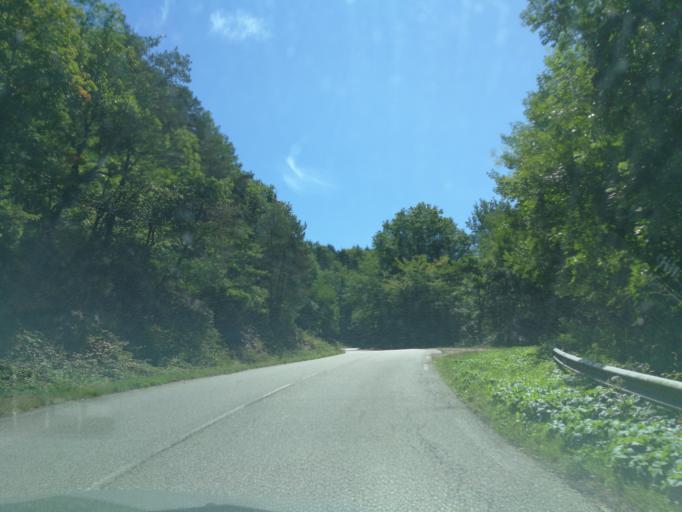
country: FR
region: Limousin
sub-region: Departement de la Correze
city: Argentat
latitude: 45.0583
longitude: 1.9459
